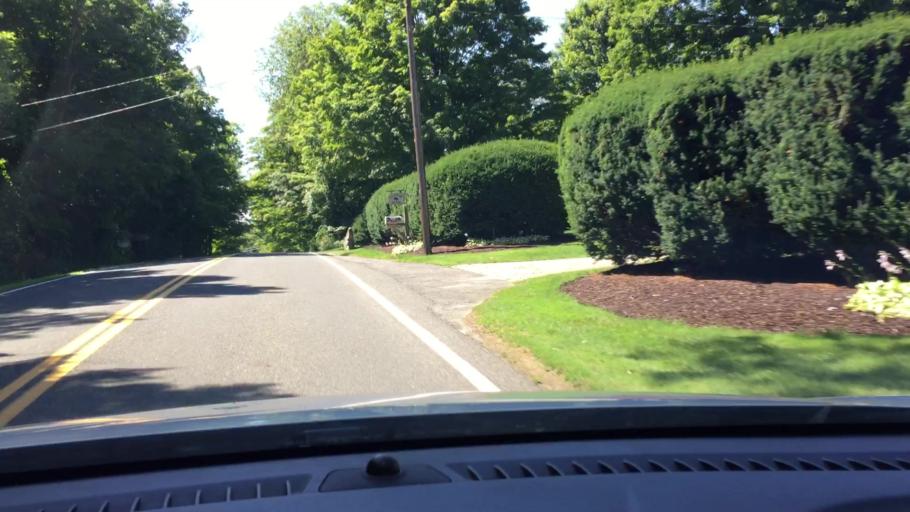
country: US
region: Massachusetts
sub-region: Berkshire County
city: Pittsfield
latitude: 42.4053
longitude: -73.2535
